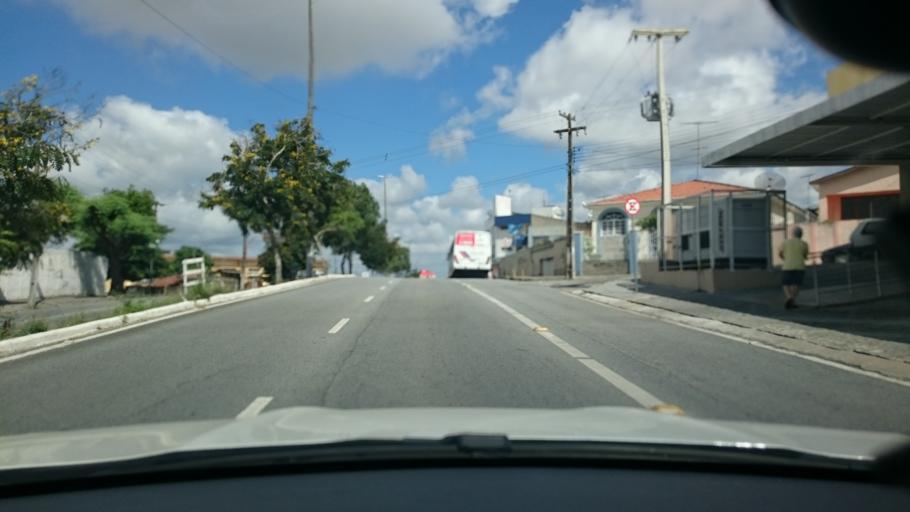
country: BR
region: Paraiba
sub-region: Campina Grande
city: Campina Grande
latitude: -7.2262
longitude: -35.8983
